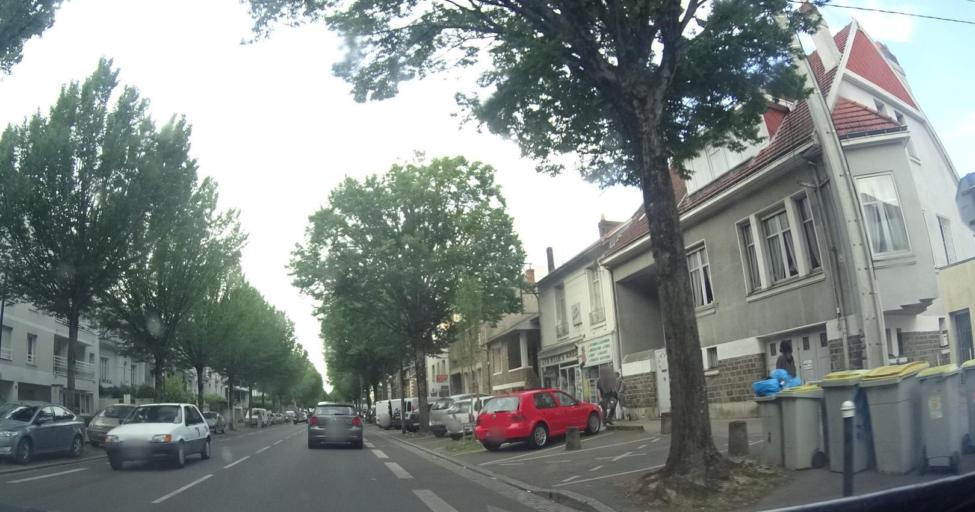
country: FR
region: Pays de la Loire
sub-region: Departement de la Loire-Atlantique
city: Nantes
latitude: 47.2354
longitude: -1.5347
